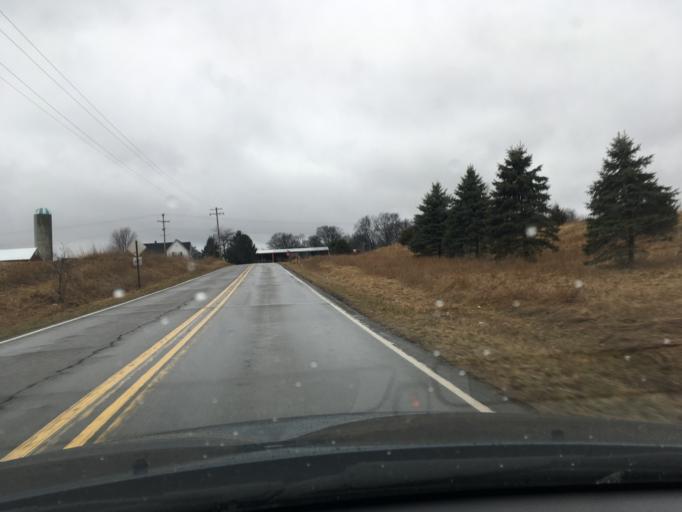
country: US
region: Michigan
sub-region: Jackson County
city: Grass Lake
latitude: 42.3110
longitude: -84.1479
